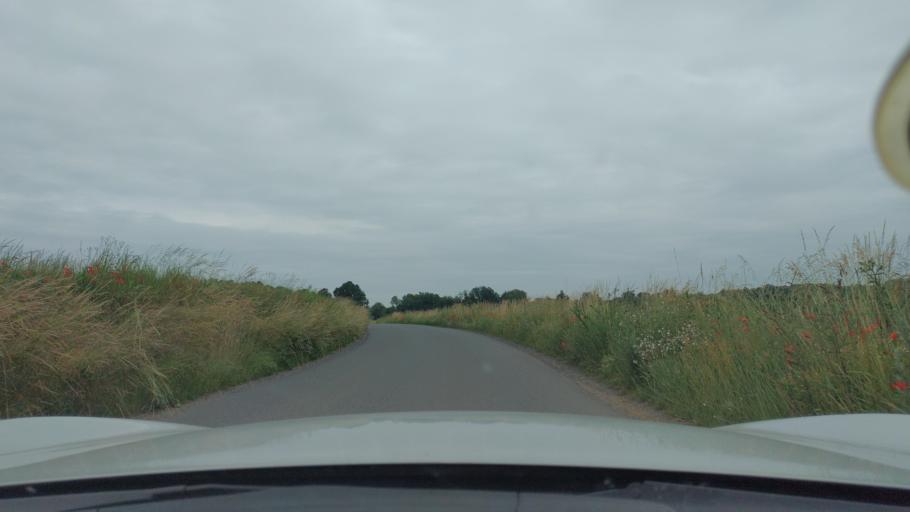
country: FR
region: Picardie
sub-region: Departement de l'Oise
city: Betz
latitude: 49.1479
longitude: 2.9628
